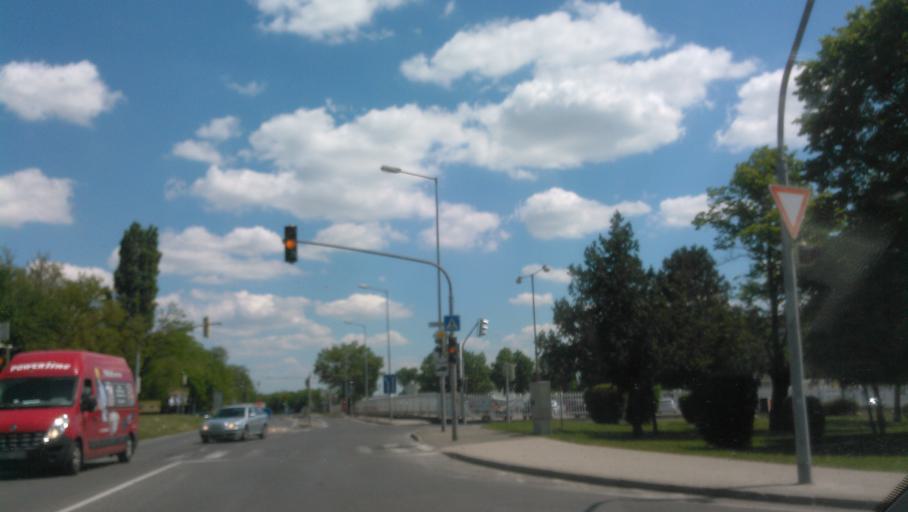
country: SK
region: Bratislavsky
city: Bratislava
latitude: 48.1294
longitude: 17.1765
